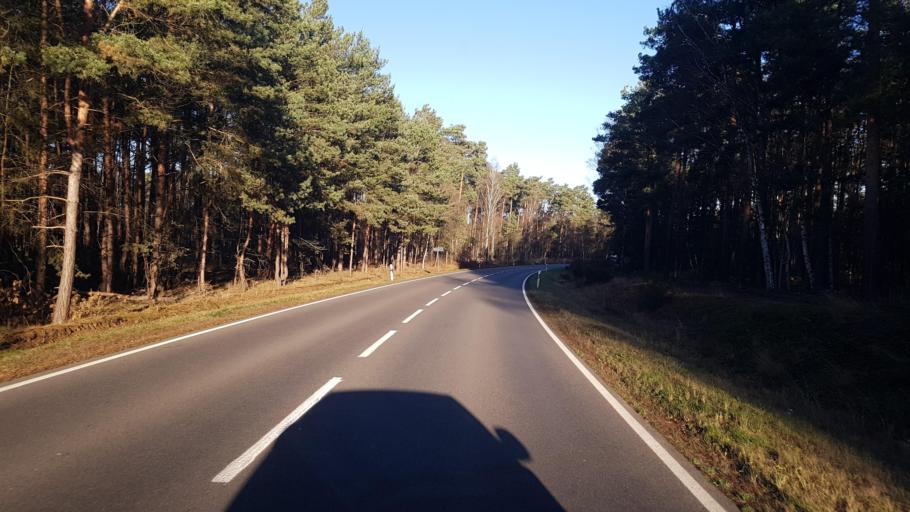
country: DE
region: Brandenburg
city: Heinersbruck
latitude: 51.7166
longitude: 14.4589
